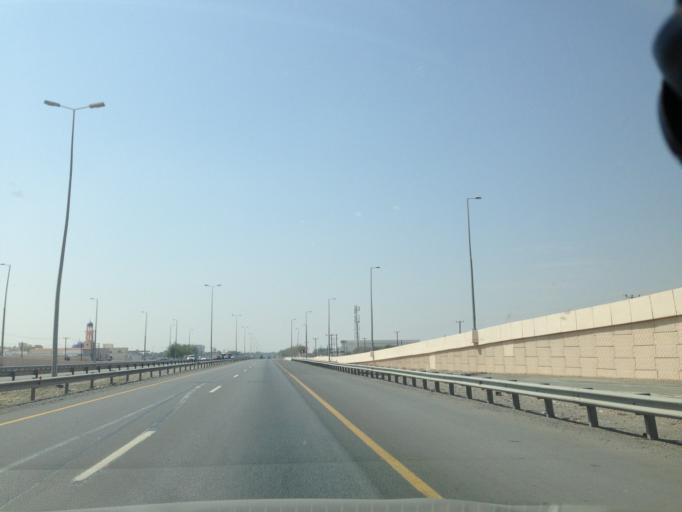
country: OM
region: Al Batinah
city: Barka'
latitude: 23.6629
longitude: 57.9471
